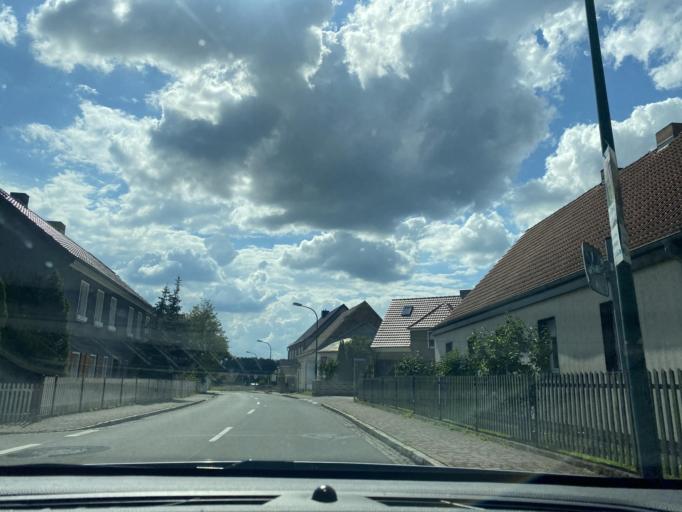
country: DE
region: Saxony
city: Boxberg
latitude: 51.4083
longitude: 14.5764
